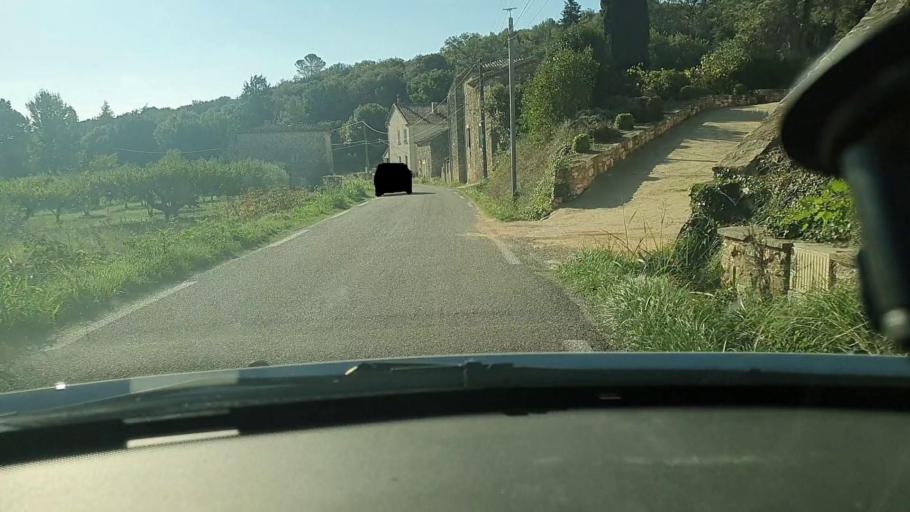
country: FR
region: Languedoc-Roussillon
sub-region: Departement du Gard
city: Goudargues
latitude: 44.2279
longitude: 4.4488
